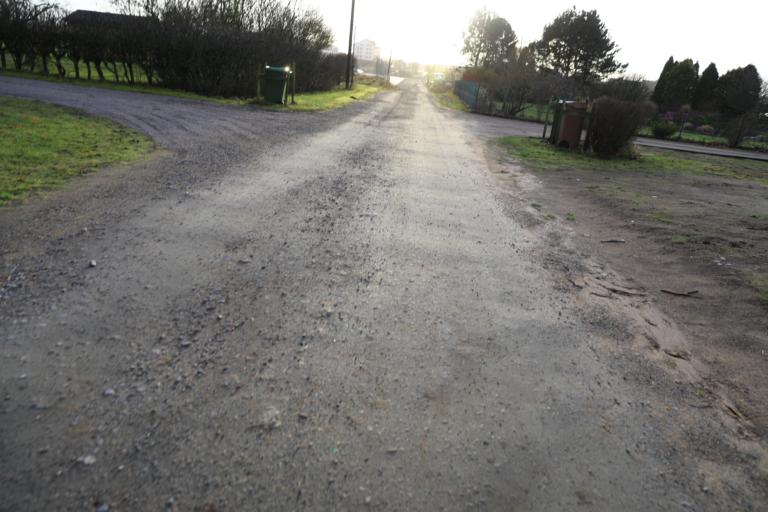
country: SE
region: Halland
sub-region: Varbergs Kommun
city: Traslovslage
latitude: 57.0919
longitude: 12.2838
